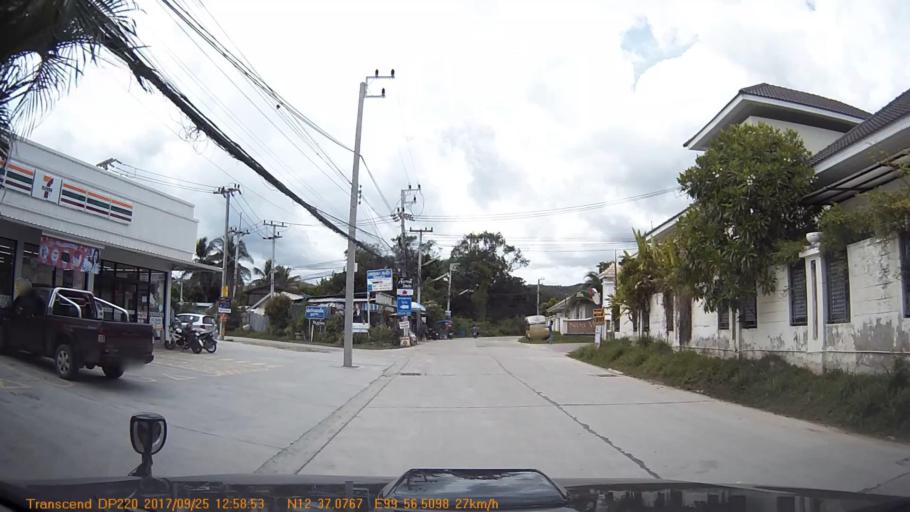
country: TH
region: Prachuap Khiri Khan
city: Hua Hin
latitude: 12.6179
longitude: 99.9415
